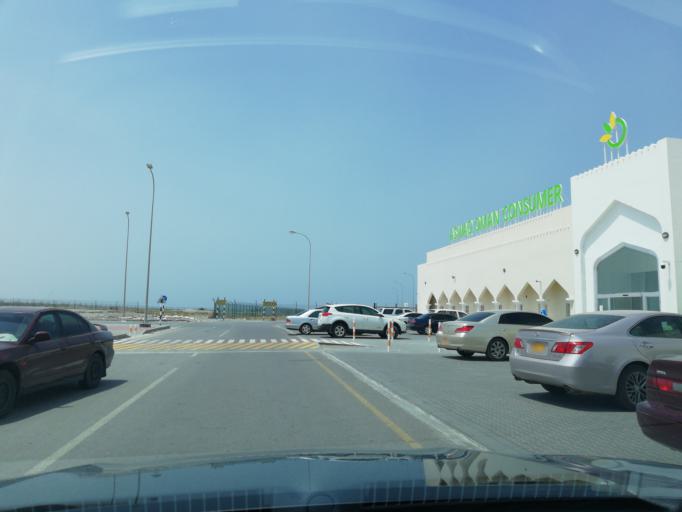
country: OM
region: Al Batinah
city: Shinas
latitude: 24.7478
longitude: 56.4696
